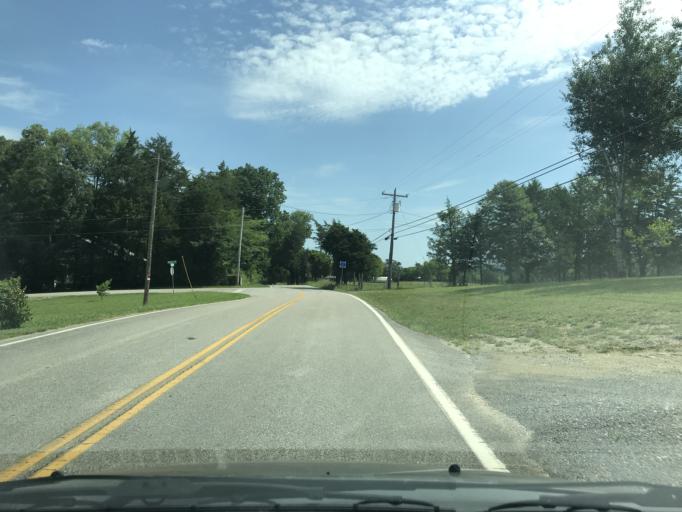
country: US
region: Tennessee
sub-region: Hamilton County
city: Lakesite
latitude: 35.2114
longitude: -85.0204
